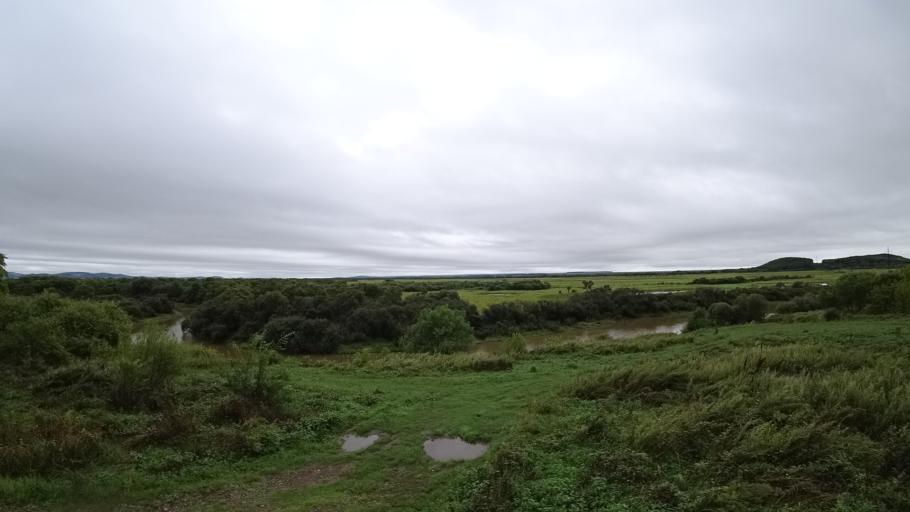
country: RU
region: Primorskiy
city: Monastyrishche
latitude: 44.2616
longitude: 132.4057
